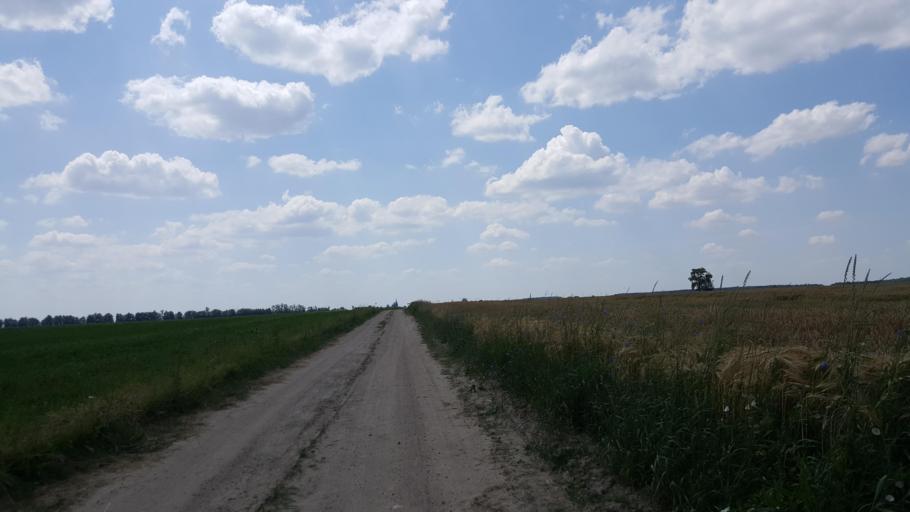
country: BY
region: Brest
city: Kamyanyets
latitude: 52.4045
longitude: 23.7726
